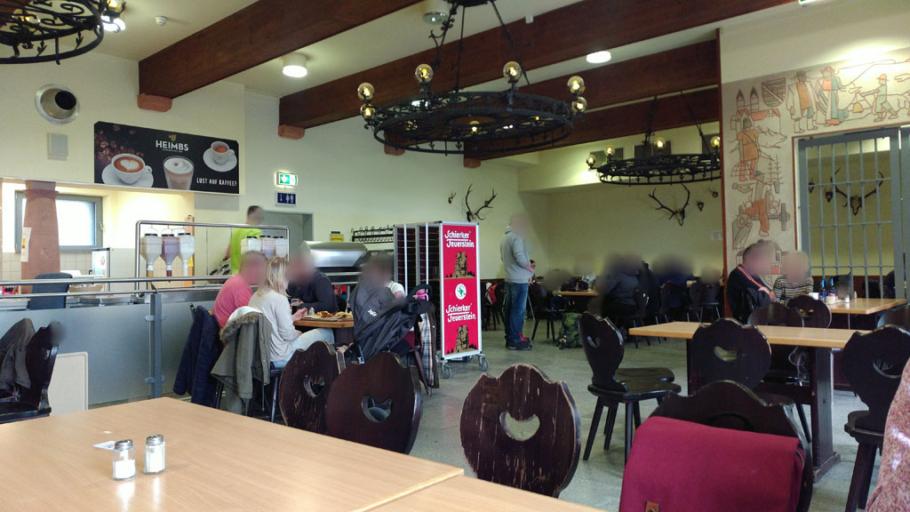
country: DE
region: Lower Saxony
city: Braunlage
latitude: 51.8001
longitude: 10.6150
